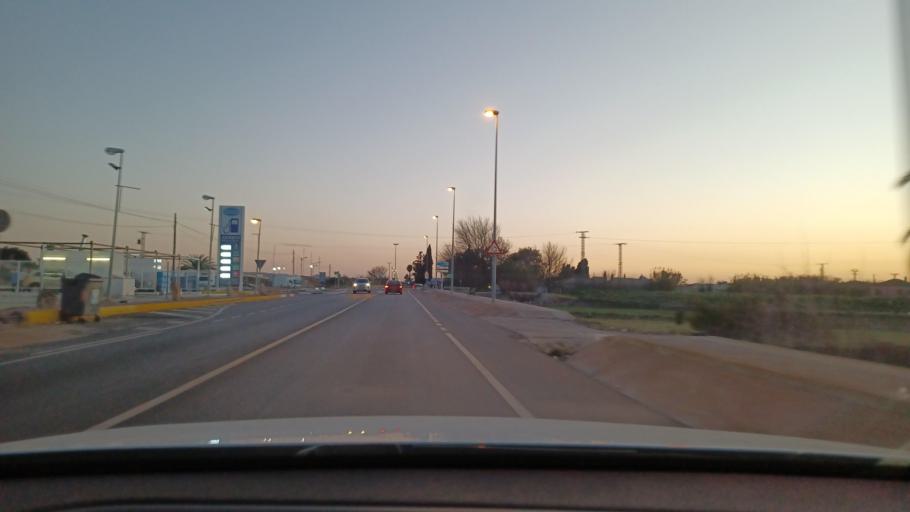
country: ES
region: Valencia
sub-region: Provincia de Alicante
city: Dolores
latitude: 38.1313
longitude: -0.7759
